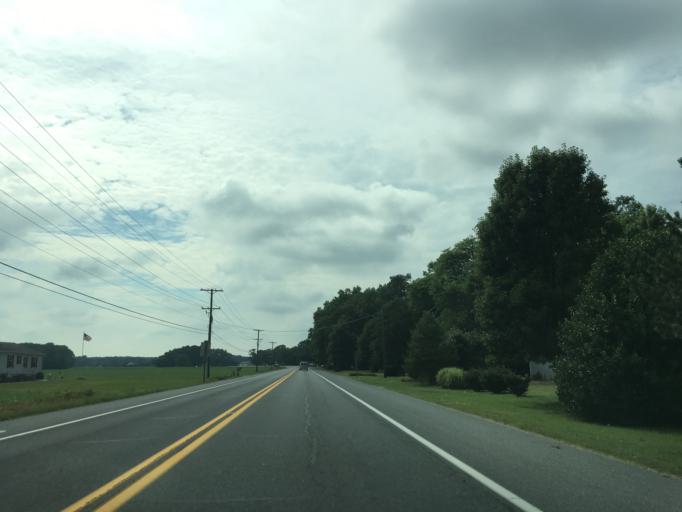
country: US
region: Delaware
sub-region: Sussex County
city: Long Neck
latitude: 38.5560
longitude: -75.1598
